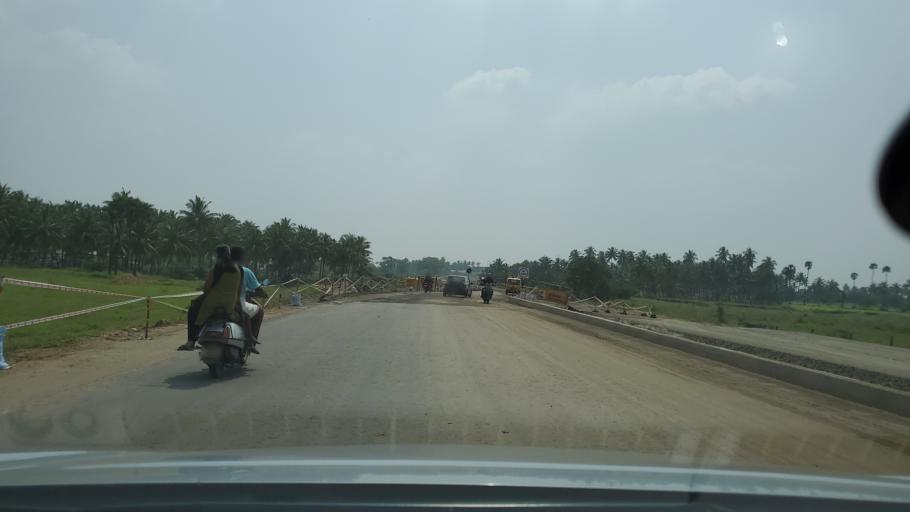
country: IN
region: Tamil Nadu
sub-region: Tiruppur
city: Kangayam
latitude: 10.9552
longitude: 77.4317
